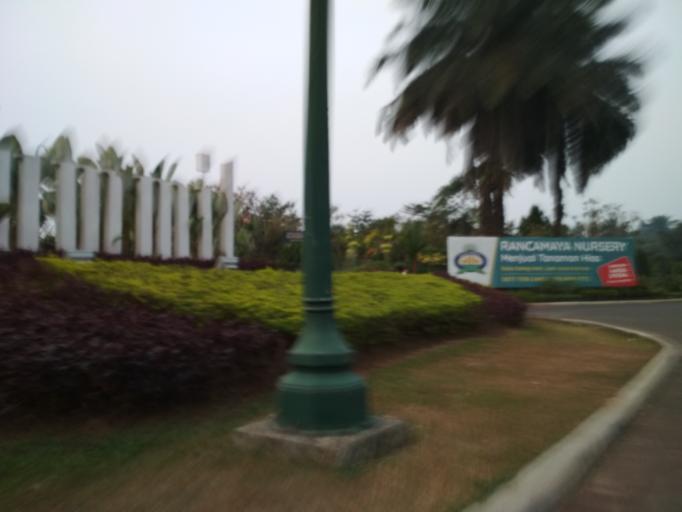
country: ID
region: West Java
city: Caringin
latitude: -6.6619
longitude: 106.8365
